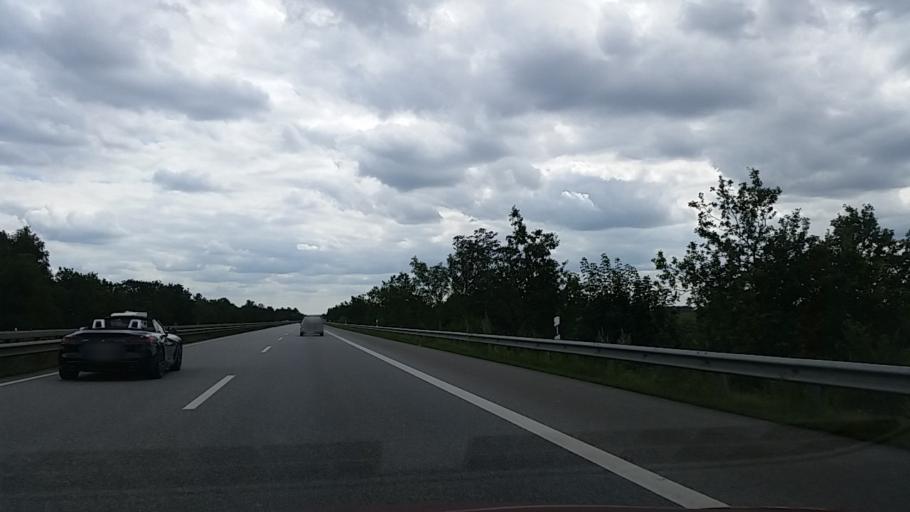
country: DE
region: Lower Saxony
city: Driftsethe
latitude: 53.3969
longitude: 8.5783
